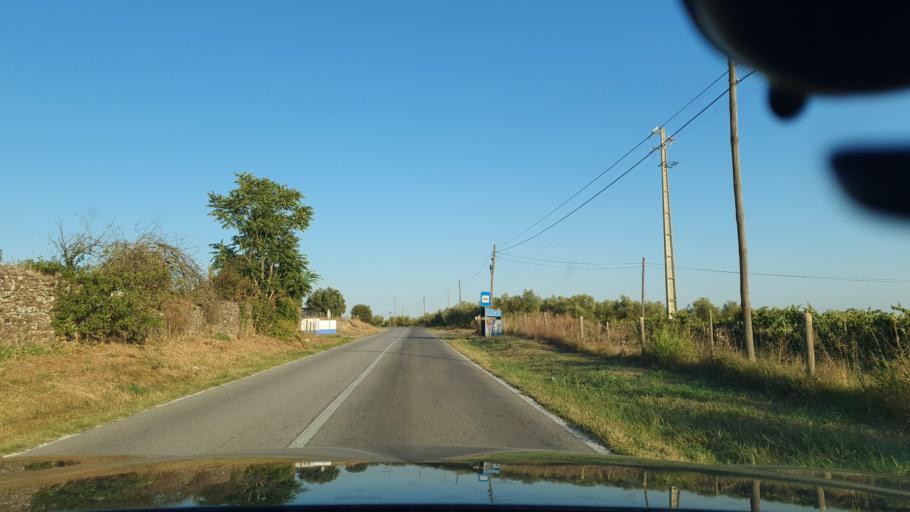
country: PT
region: Evora
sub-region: Estremoz
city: Estremoz
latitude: 38.8923
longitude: -7.6617
